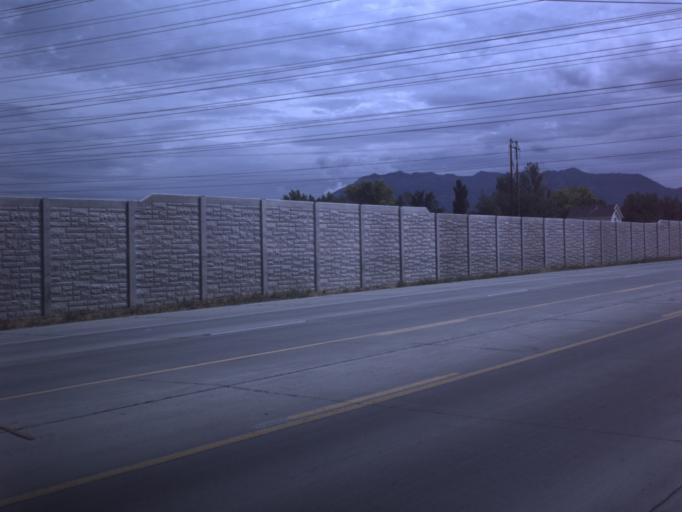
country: US
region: Utah
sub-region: Davis County
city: Syracuse
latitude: 41.1105
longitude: -112.0537
